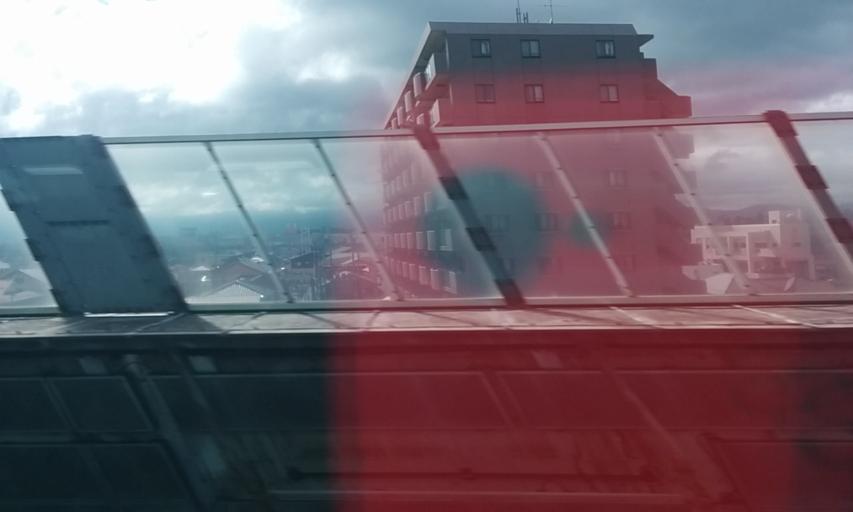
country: JP
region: Fukushima
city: Koriyama
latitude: 37.3767
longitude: 140.3830
